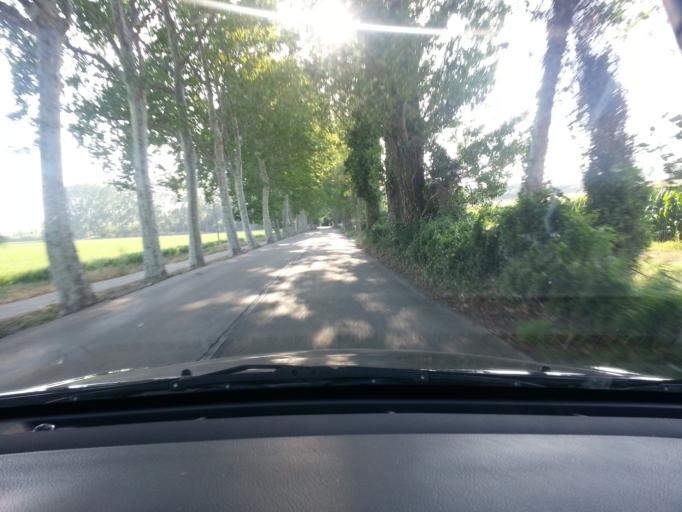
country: ES
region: Catalonia
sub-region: Provincia de Girona
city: Pals
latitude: 42.0127
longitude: 3.1709
